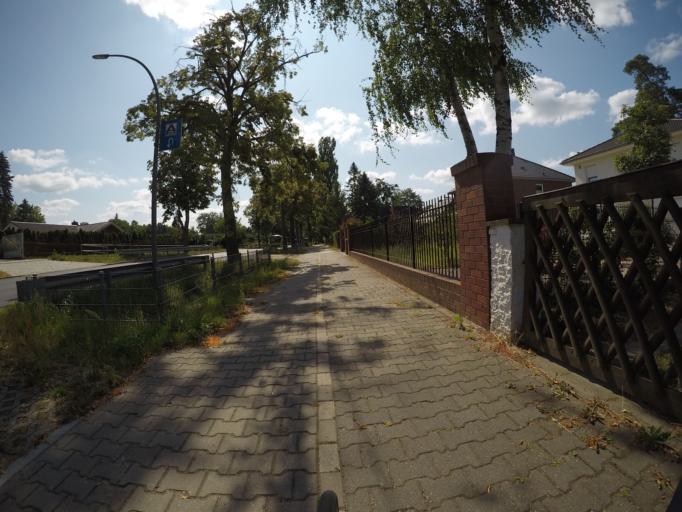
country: DE
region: Berlin
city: Kladow
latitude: 52.4632
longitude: 13.1313
